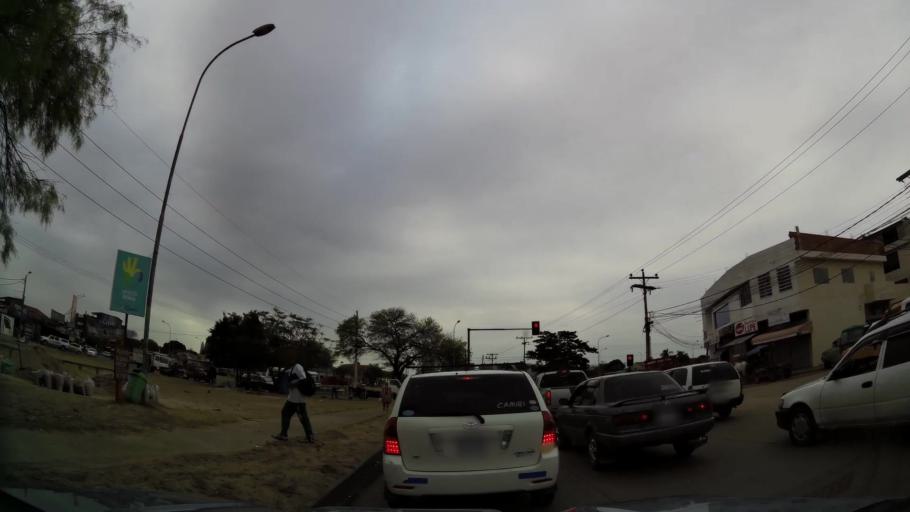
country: BO
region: Santa Cruz
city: Santa Cruz de la Sierra
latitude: -17.7994
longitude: -63.1502
